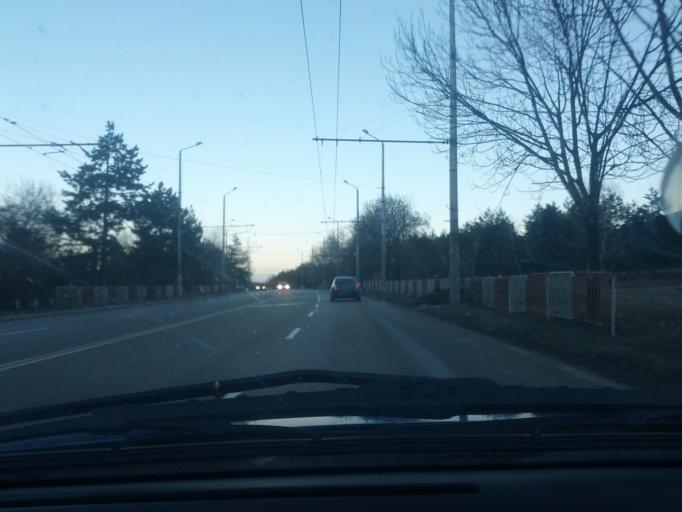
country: BG
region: Vratsa
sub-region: Obshtina Vratsa
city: Vratsa
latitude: 43.1862
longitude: 23.5831
